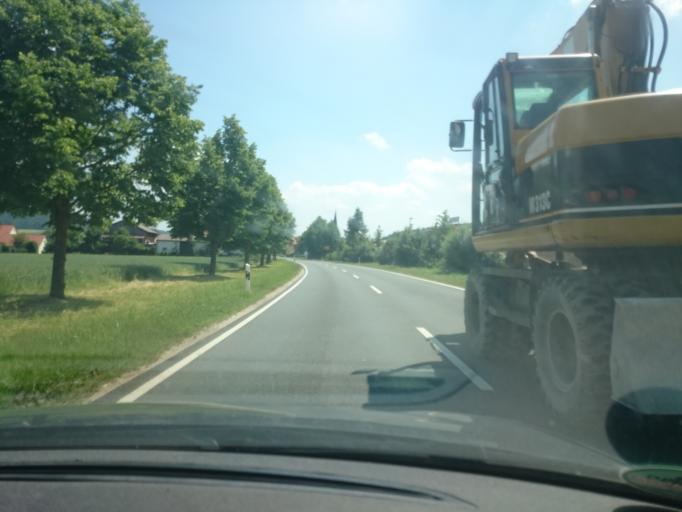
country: DE
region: Bavaria
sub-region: Regierungsbezirk Mittelfranken
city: Thalmassing
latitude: 49.1485
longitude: 11.2592
